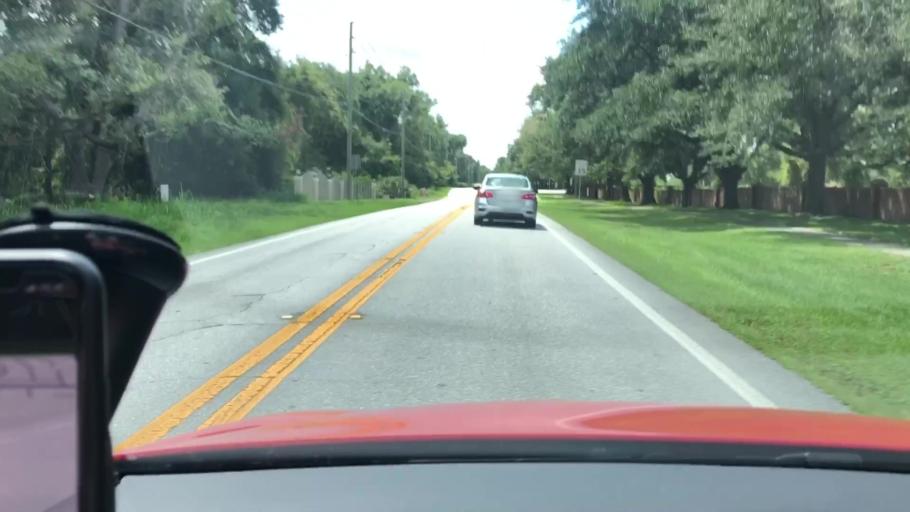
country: US
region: Florida
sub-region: Lake County
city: Eustis
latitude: 28.8447
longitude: -81.6545
